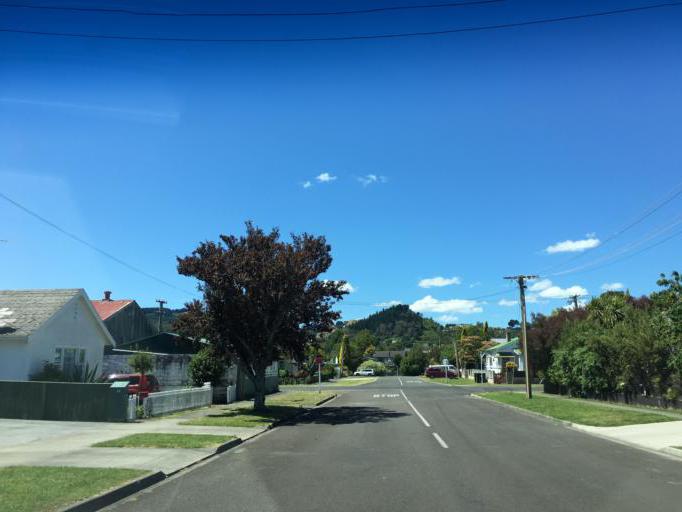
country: NZ
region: Gisborne
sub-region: Gisborne District
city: Gisborne
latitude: -38.6603
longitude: 178.0238
